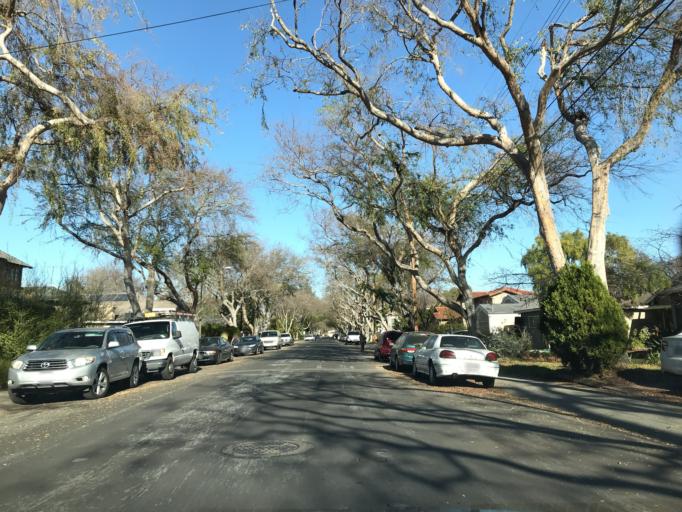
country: US
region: California
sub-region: Santa Clara County
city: Palo Alto
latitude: 37.4346
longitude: -122.1226
